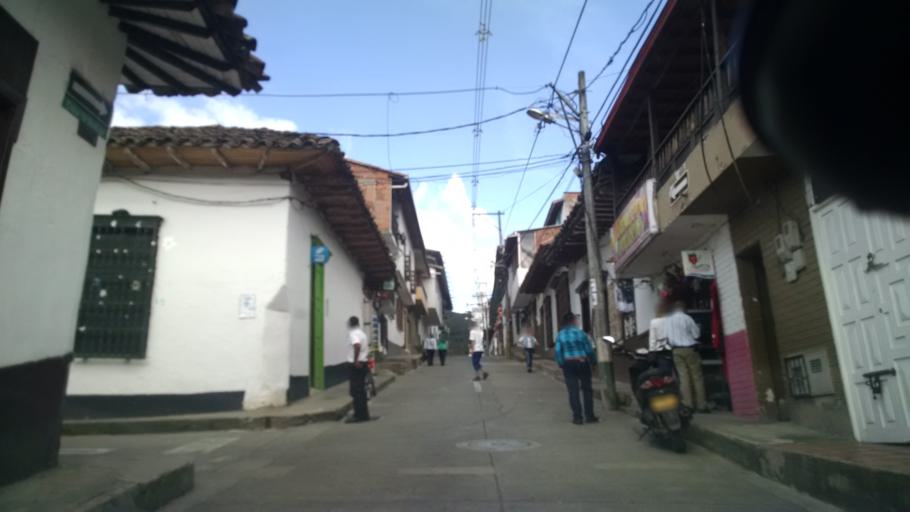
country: CO
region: Antioquia
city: El Retiro
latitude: 6.0569
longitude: -75.5037
